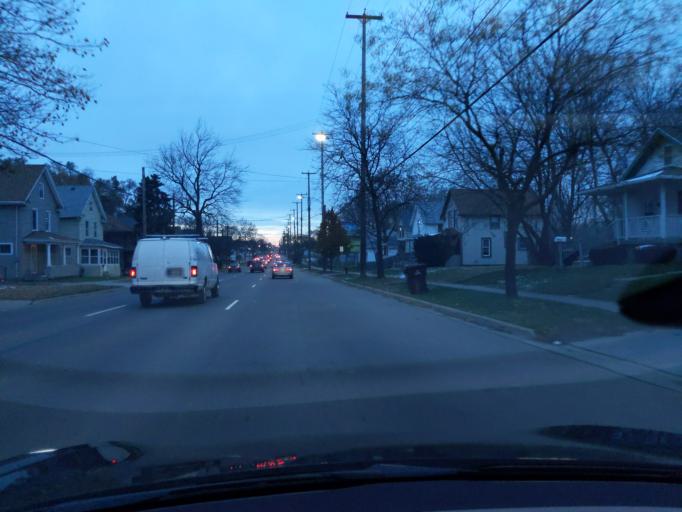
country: US
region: Michigan
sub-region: Ingham County
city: Lansing
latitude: 42.7447
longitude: -84.5446
